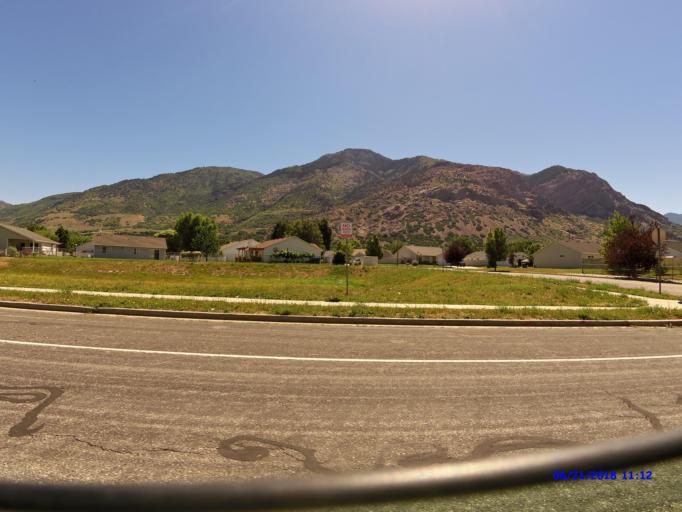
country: US
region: Utah
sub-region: Weber County
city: North Ogden
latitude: 41.2830
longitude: -111.9590
